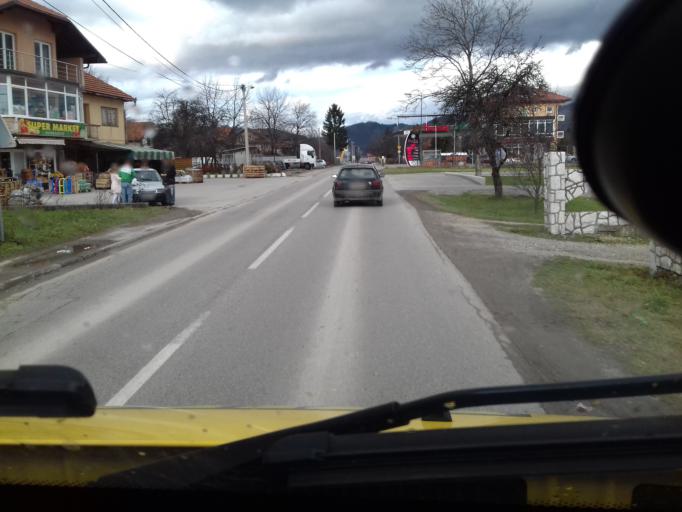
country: BA
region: Federation of Bosnia and Herzegovina
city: Gornje Mostre
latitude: 44.0155
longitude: 18.1405
